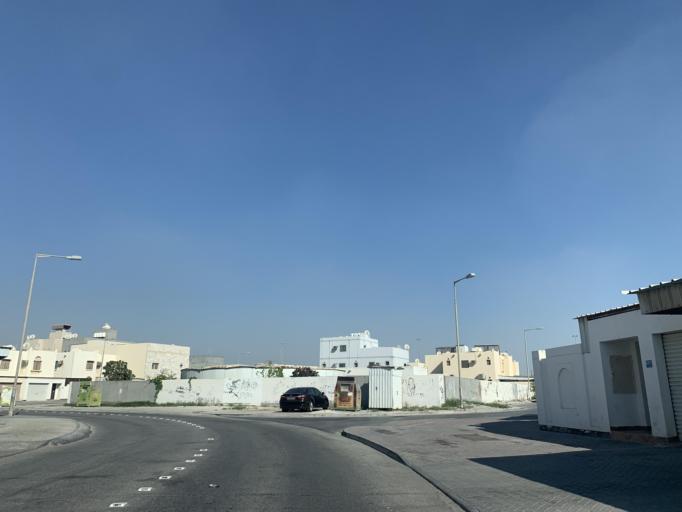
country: BH
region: Central Governorate
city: Madinat Hamad
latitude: 26.1153
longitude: 50.5092
